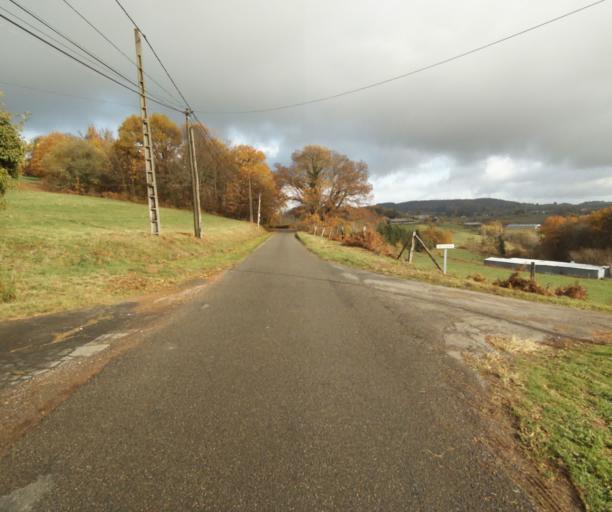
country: FR
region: Limousin
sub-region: Departement de la Correze
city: Sainte-Fereole
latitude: 45.2199
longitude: 1.6251
